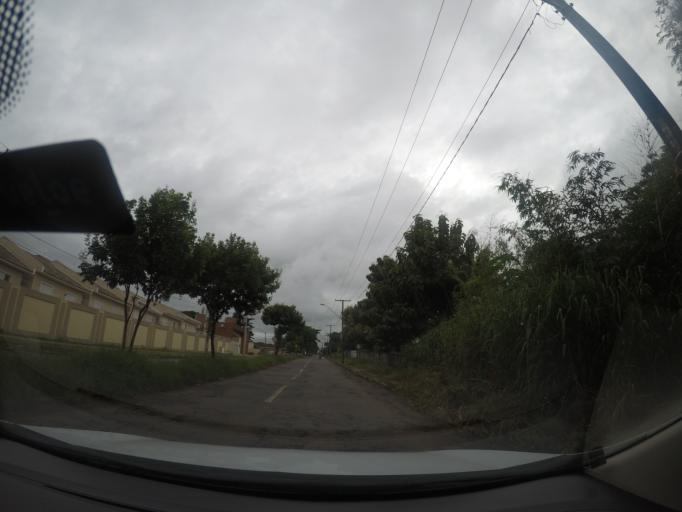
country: BR
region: Goias
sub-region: Goiania
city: Goiania
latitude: -16.7309
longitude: -49.2826
